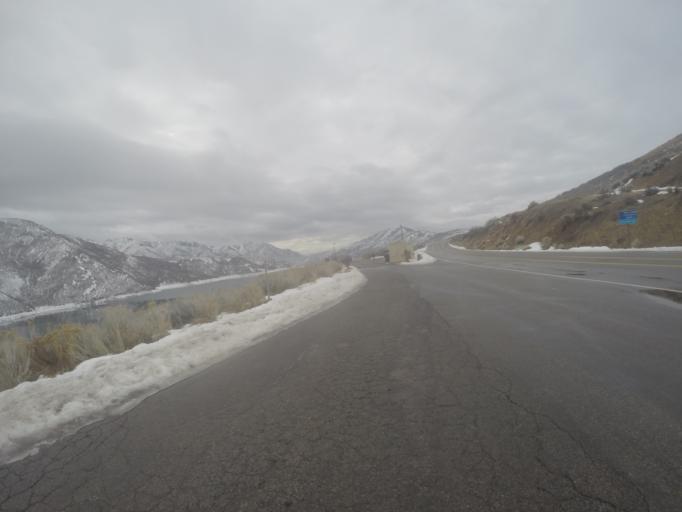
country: US
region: Utah
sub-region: Summit County
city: Summit Park
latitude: 40.7790
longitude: -111.6877
